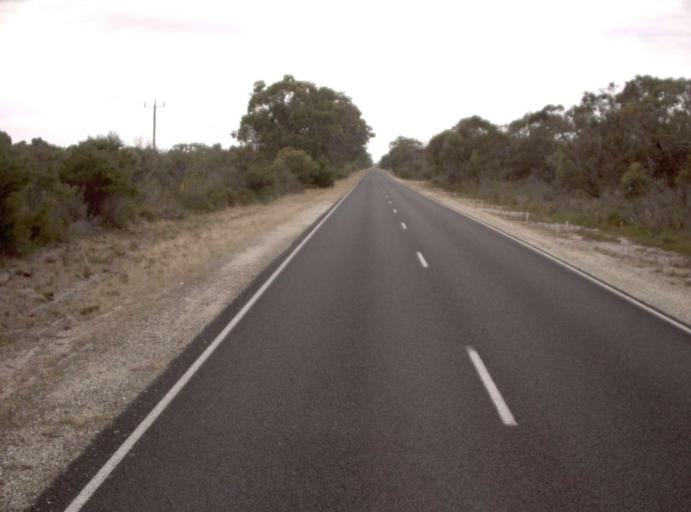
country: AU
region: Victoria
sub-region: Wellington
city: Sale
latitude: -38.1366
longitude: 147.4134
